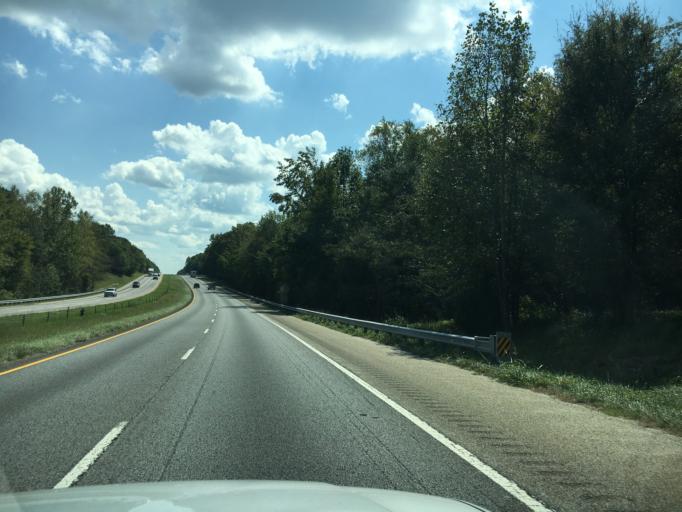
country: US
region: South Carolina
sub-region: Spartanburg County
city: Roebuck
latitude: 34.8853
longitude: -81.9934
